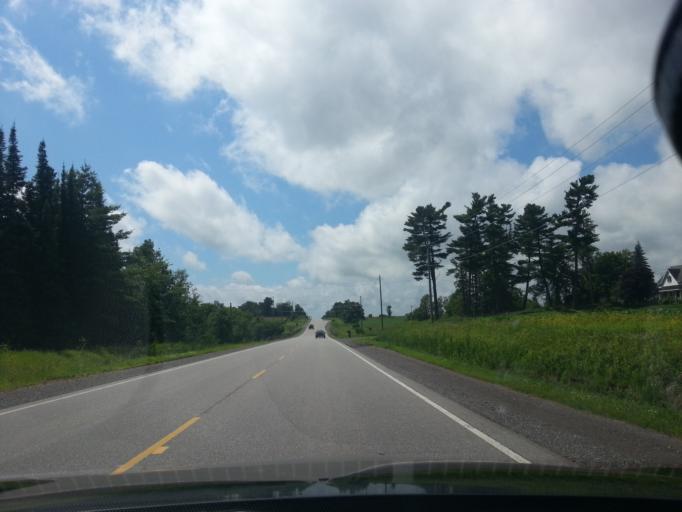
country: CA
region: Ontario
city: Renfrew
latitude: 45.5209
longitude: -76.8588
